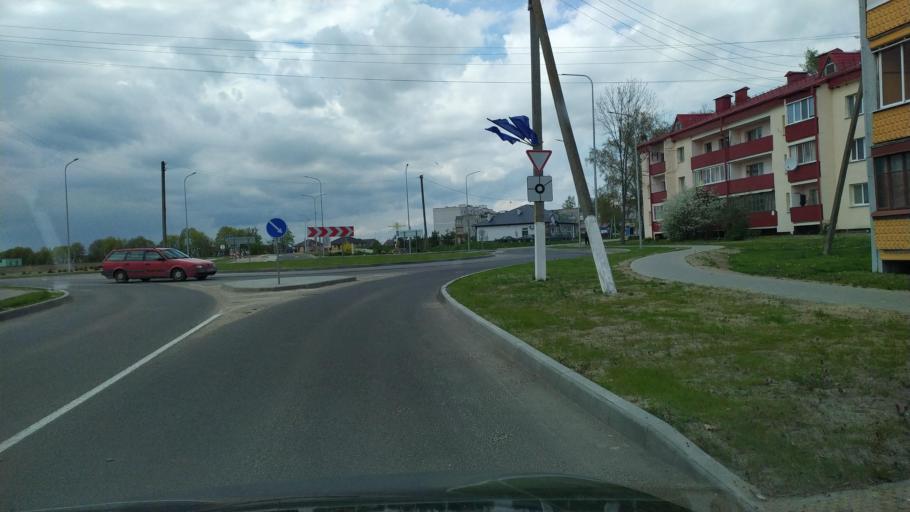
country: BY
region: Brest
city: Pruzhany
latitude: 52.5587
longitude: 24.4284
